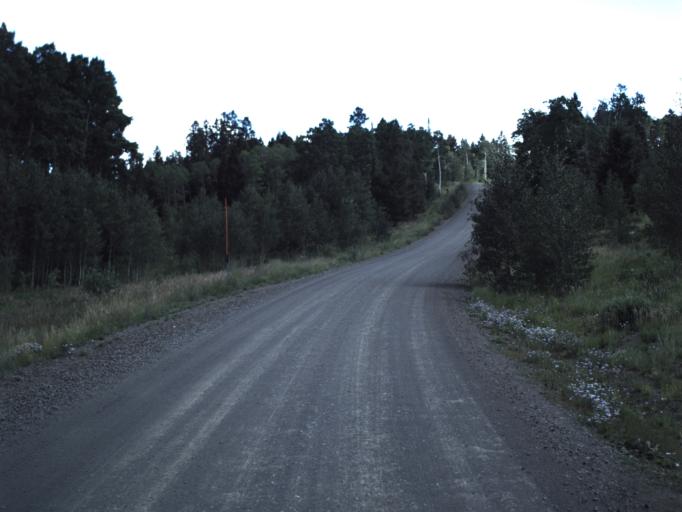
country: US
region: Utah
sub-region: Piute County
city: Junction
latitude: 38.2533
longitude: -112.3351
